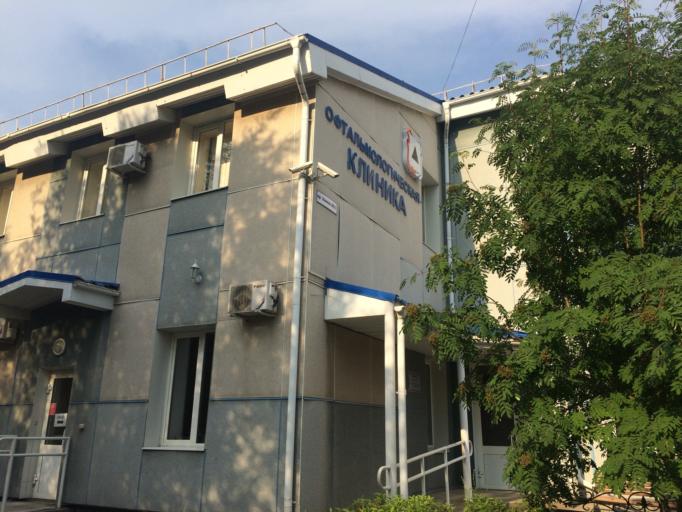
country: RU
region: Chelyabinsk
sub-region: Gorod Magnitogorsk
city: Magnitogorsk
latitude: 53.4033
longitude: 58.9837
